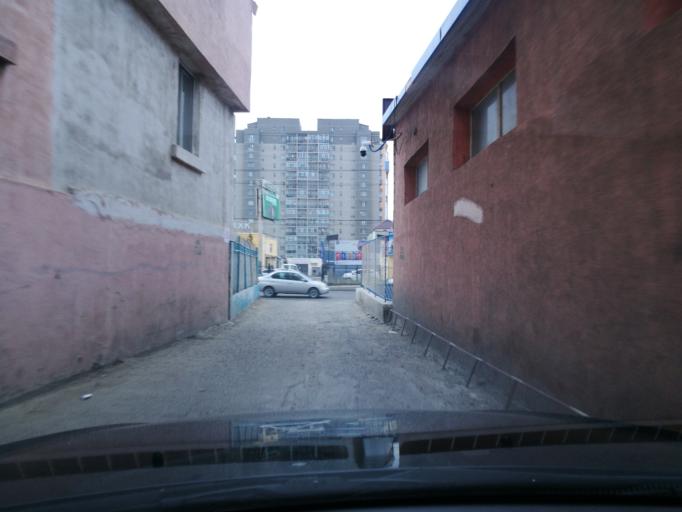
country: MN
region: Ulaanbaatar
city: Ulaanbaatar
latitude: 47.9291
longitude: 106.9124
